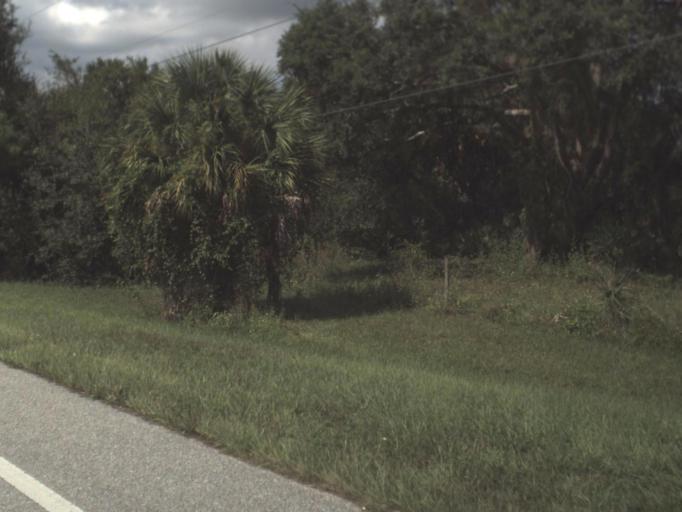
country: US
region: Florida
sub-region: Sarasota County
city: Plantation
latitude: 27.0819
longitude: -82.3323
